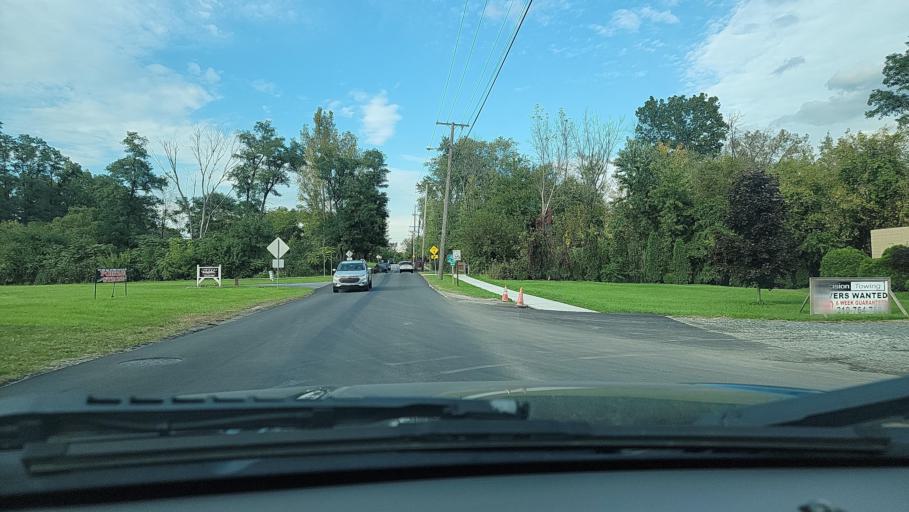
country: US
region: Indiana
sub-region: Porter County
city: Portage
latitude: 41.5848
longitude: -87.1687
